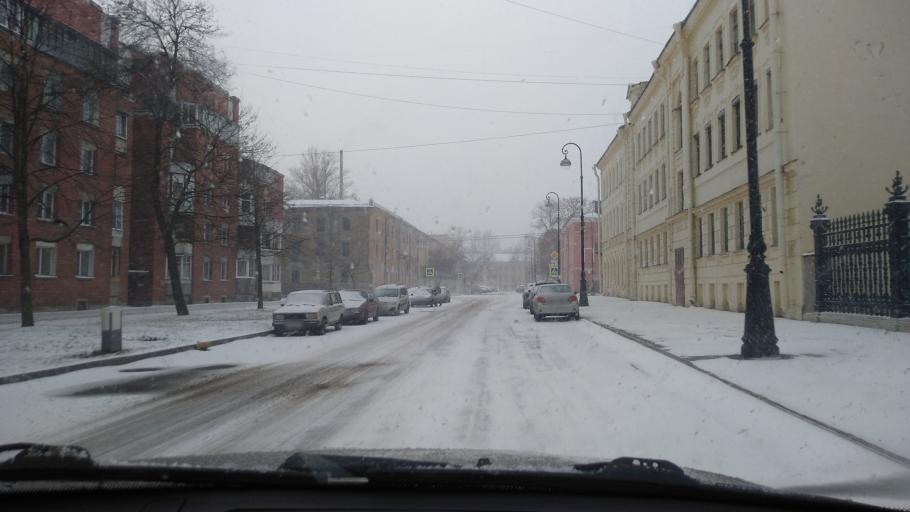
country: RU
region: St.-Petersburg
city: Kronshtadt
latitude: 59.9878
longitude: 29.7749
